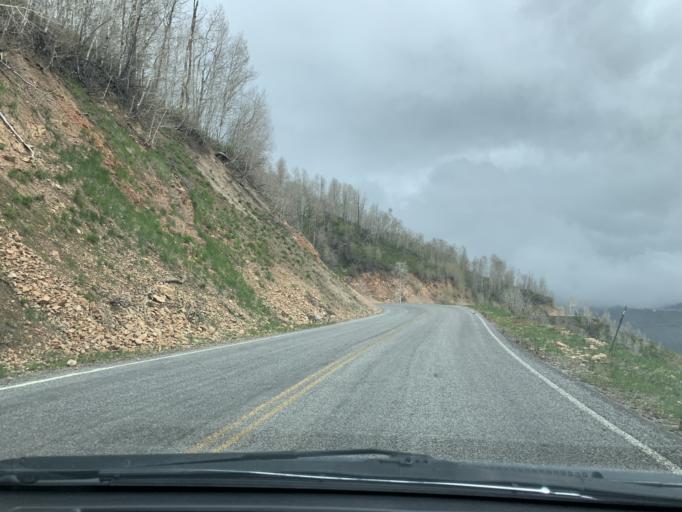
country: US
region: Utah
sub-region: Utah County
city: Elk Ridge
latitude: 39.8707
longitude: -111.6863
